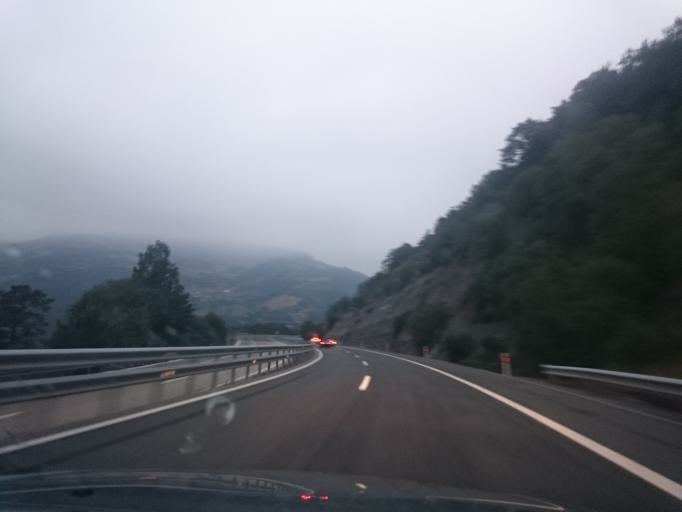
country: ES
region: Asturias
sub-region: Province of Asturias
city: Pola de Lena
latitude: 43.0557
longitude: -5.8210
